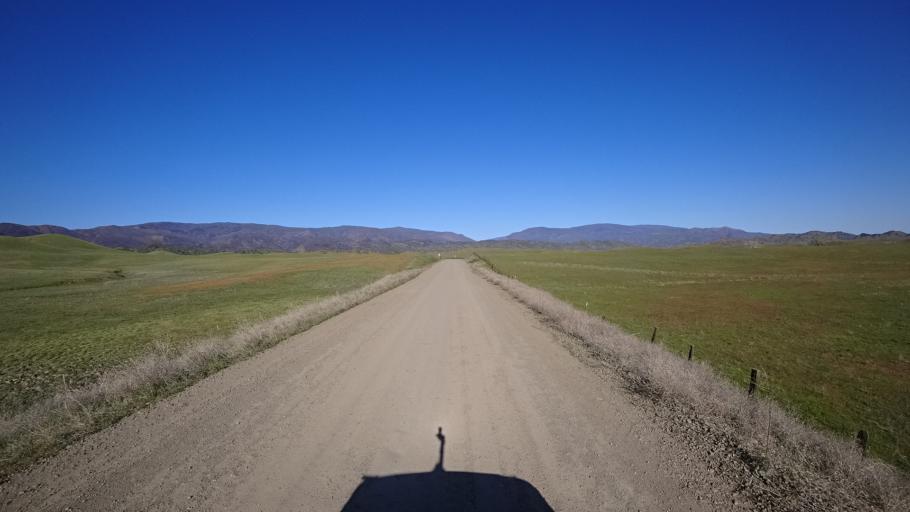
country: US
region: California
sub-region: Tehama County
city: Rancho Tehama Reserve
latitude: 39.7960
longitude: -122.5477
